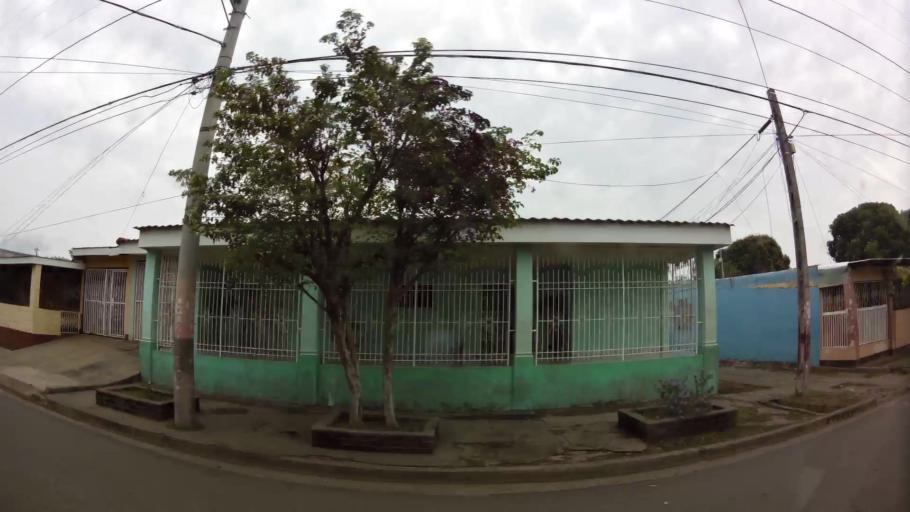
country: NI
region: Granada
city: Granada
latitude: 11.9481
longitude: -85.9481
